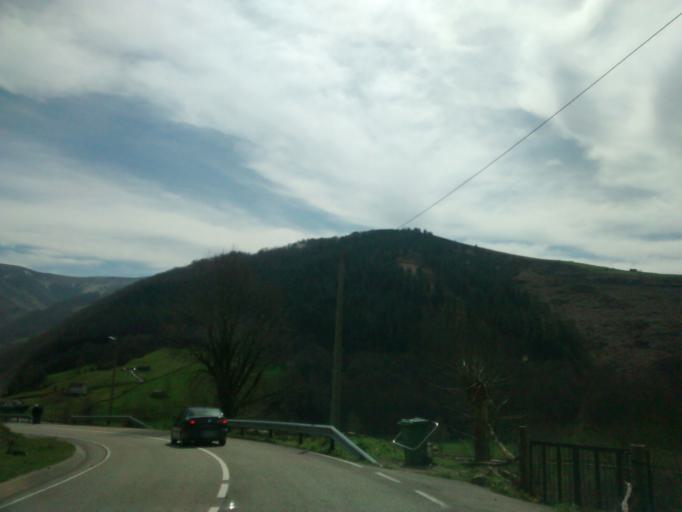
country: ES
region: Cantabria
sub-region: Provincia de Cantabria
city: Vega de Pas
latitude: 43.1619
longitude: -3.7918
